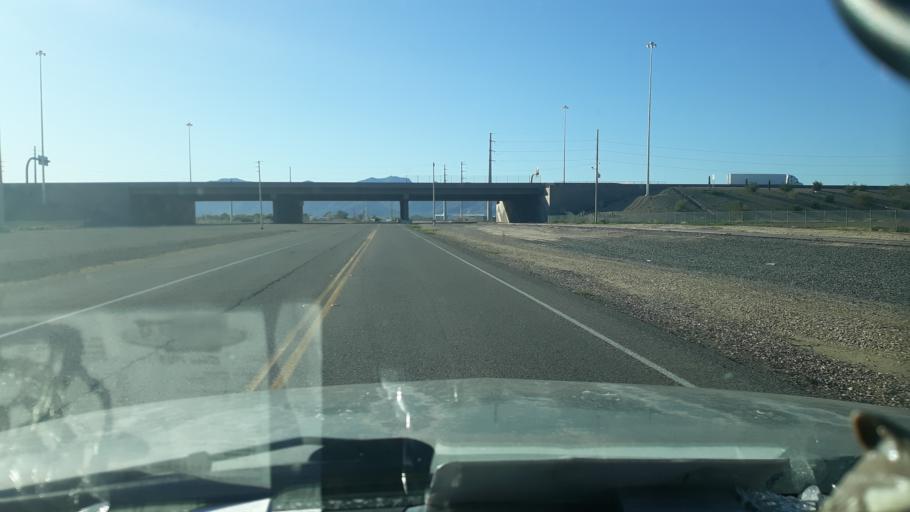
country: US
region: Arizona
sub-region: Maricopa County
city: Citrus Park
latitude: 33.5667
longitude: -112.4152
